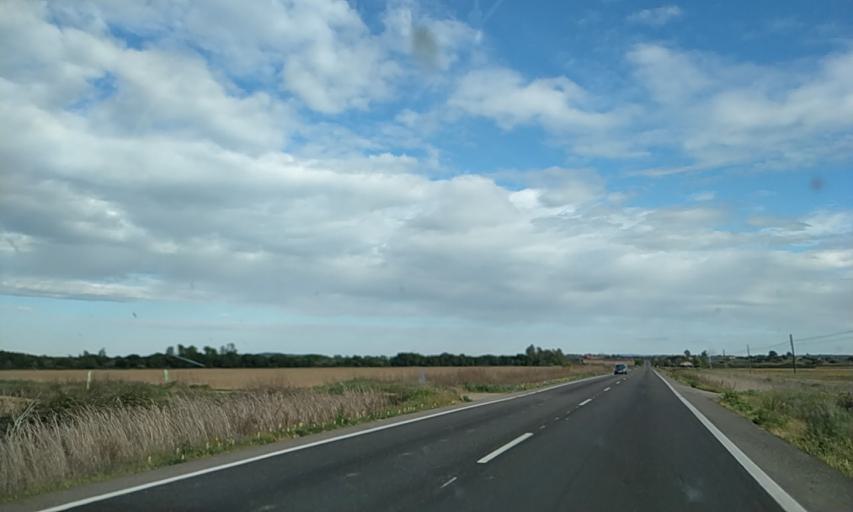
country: ES
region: Extremadura
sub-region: Provincia de Caceres
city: Huelaga
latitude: 40.0478
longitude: -6.6372
